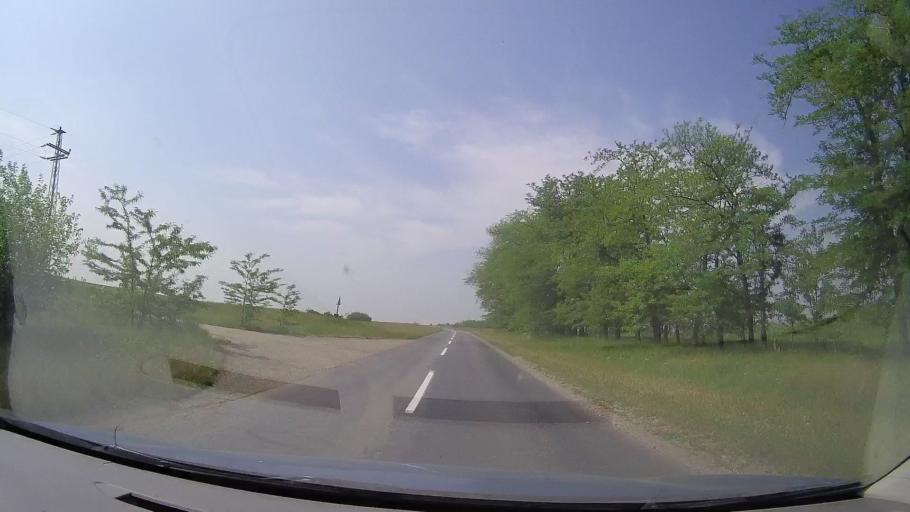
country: RS
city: Samos
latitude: 45.1890
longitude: 20.7654
